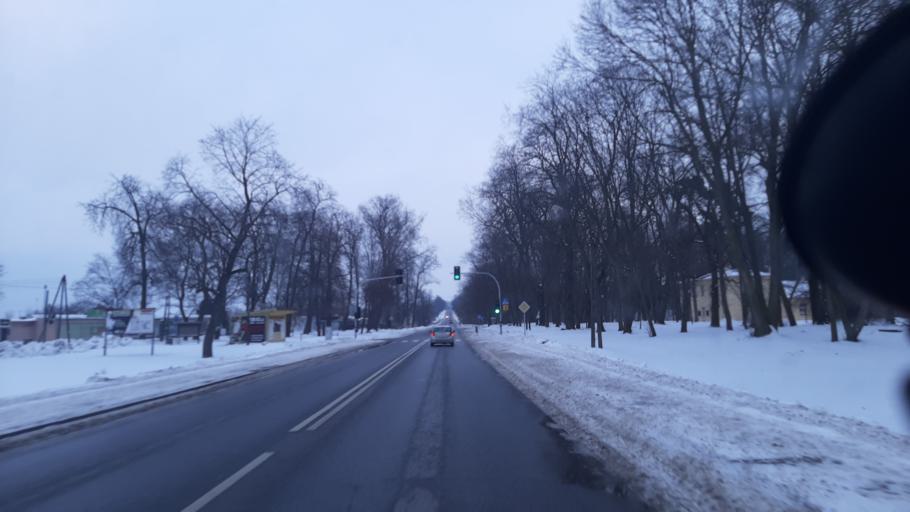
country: PL
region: Lublin Voivodeship
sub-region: Powiat lubelski
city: Garbow
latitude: 51.3544
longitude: 22.3325
